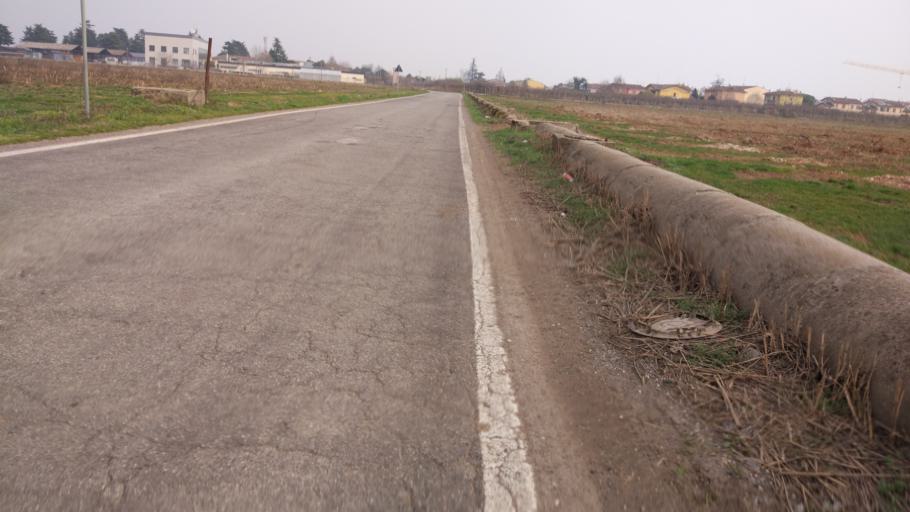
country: IT
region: Veneto
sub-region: Provincia di Verona
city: Villafranca di Verona
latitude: 45.3823
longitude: 10.8722
